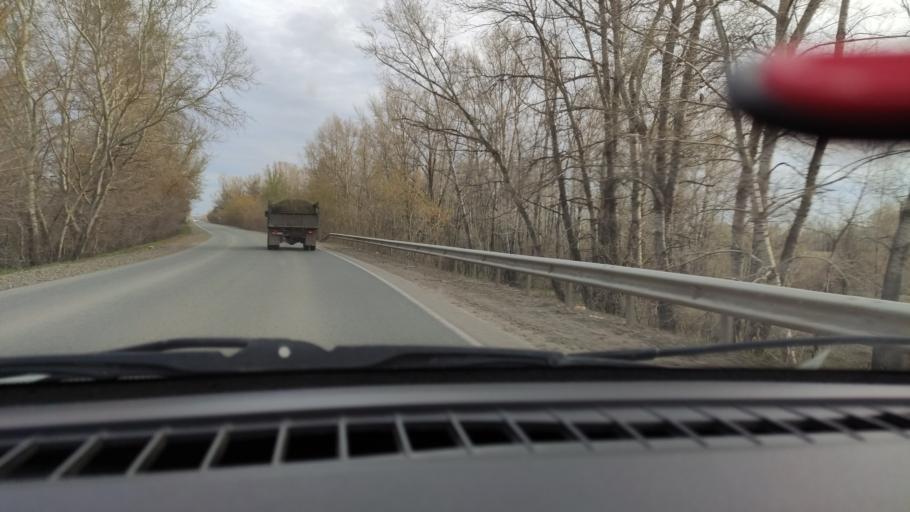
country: RU
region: Orenburg
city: Tatarskaya Kargala
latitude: 51.9319
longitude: 55.1737
